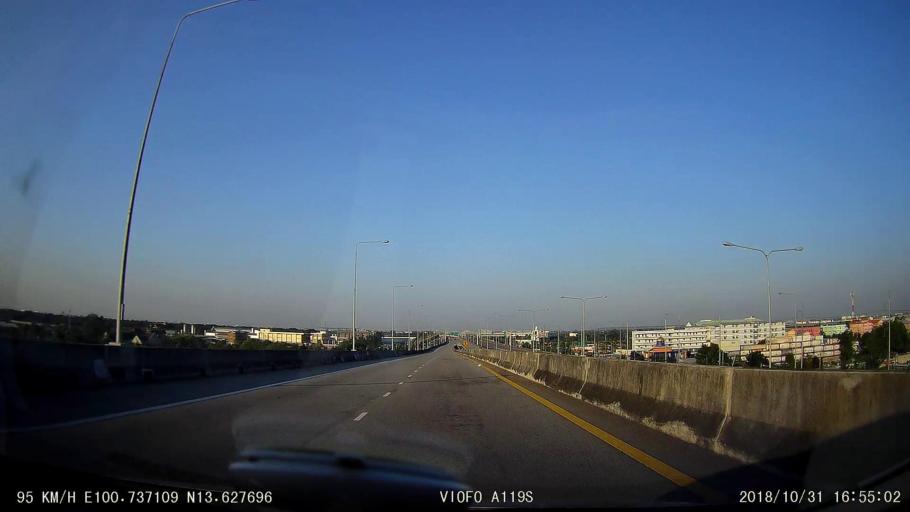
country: TH
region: Samut Prakan
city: Bang Bo District
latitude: 13.6278
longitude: 100.7371
